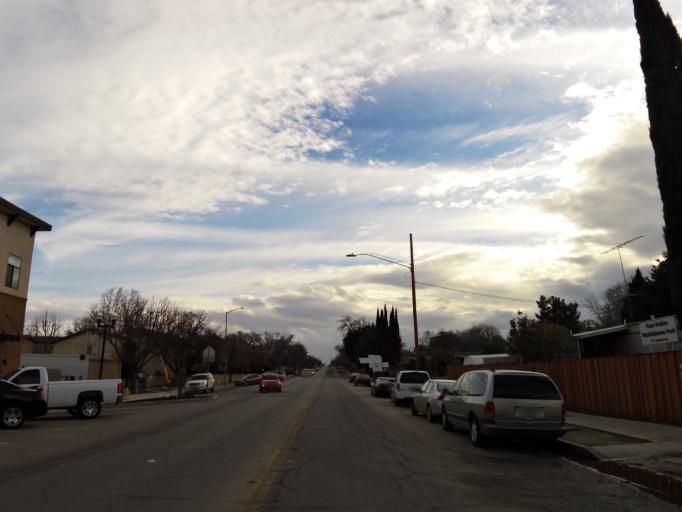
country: US
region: California
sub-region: San Luis Obispo County
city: Paso Robles
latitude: 35.6490
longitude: -120.6933
